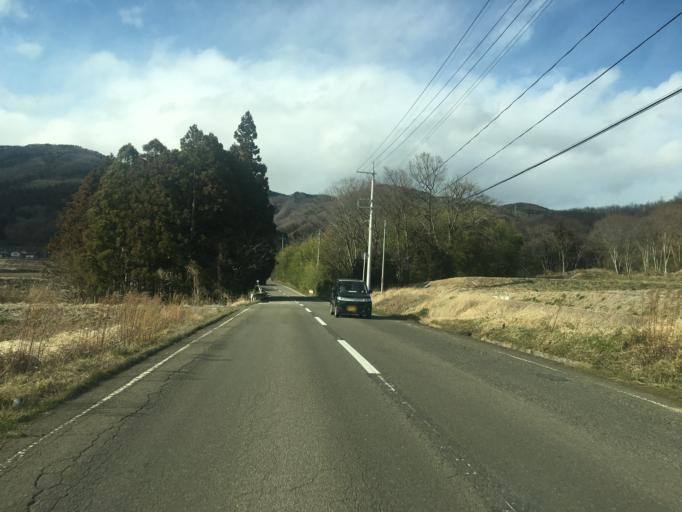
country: JP
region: Fukushima
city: Yanagawamachi-saiwaicho
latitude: 37.8987
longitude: 140.5795
